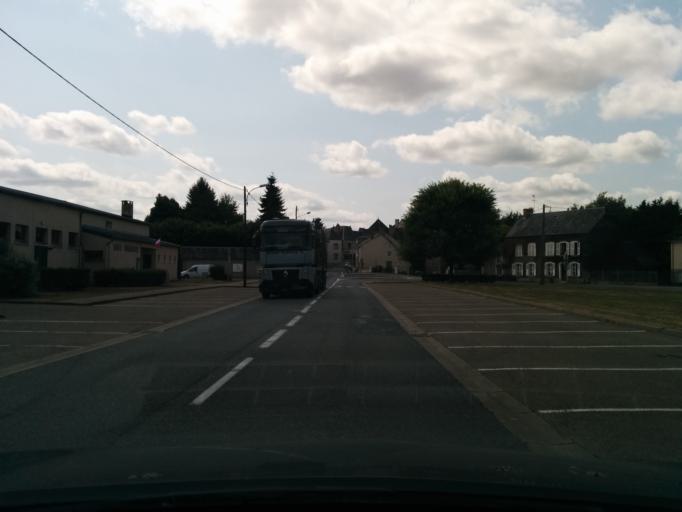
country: FR
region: Centre
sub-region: Departement du Cher
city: Henrichemont
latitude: 47.3628
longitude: 2.4373
